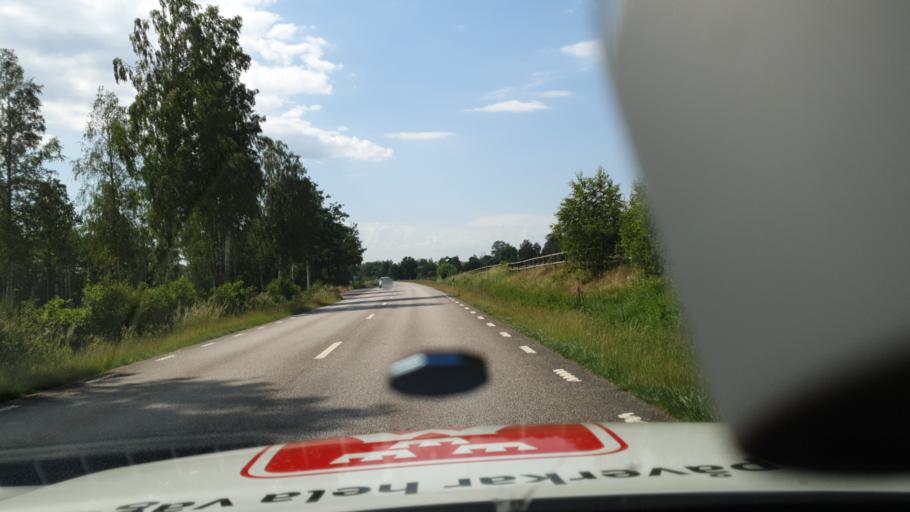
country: SE
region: Vaestra Goetaland
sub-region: Hjo Kommun
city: Hjo
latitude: 58.2200
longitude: 14.2067
